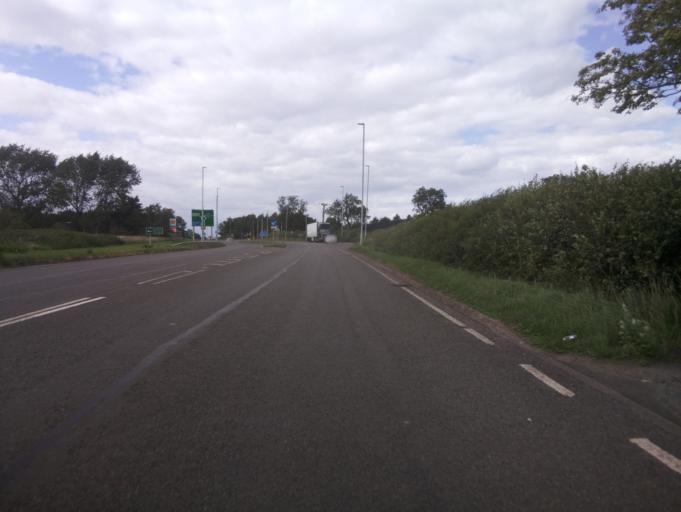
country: GB
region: England
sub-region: Leicestershire
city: Donisthorpe
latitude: 52.6862
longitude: -1.5461
